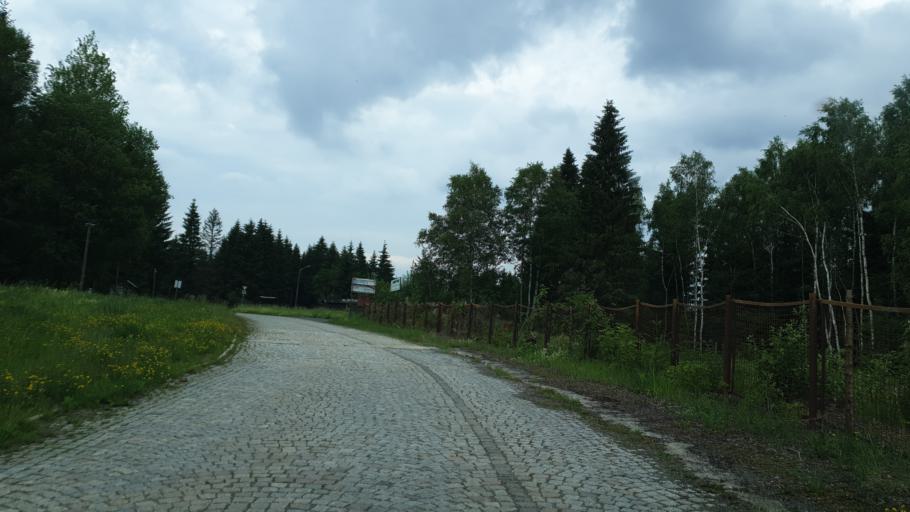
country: DE
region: Saxony
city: Tannenbergsthal
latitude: 50.4172
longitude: 12.4543
